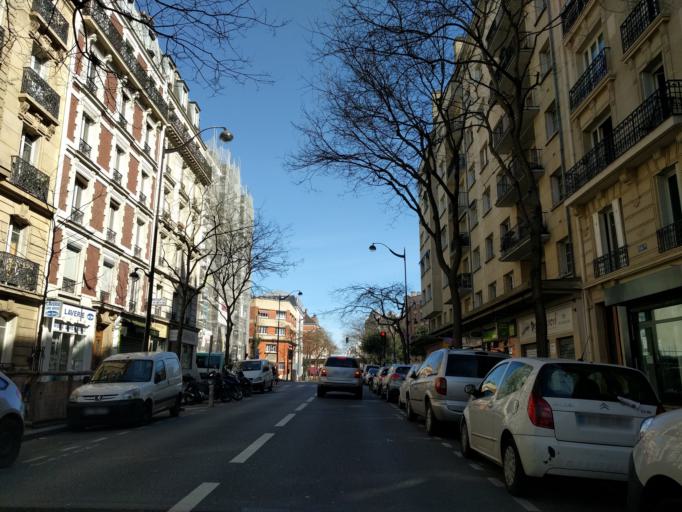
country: FR
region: Ile-de-France
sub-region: Departement du Val-de-Marne
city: Saint-Mande
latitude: 48.8393
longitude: 2.4043
